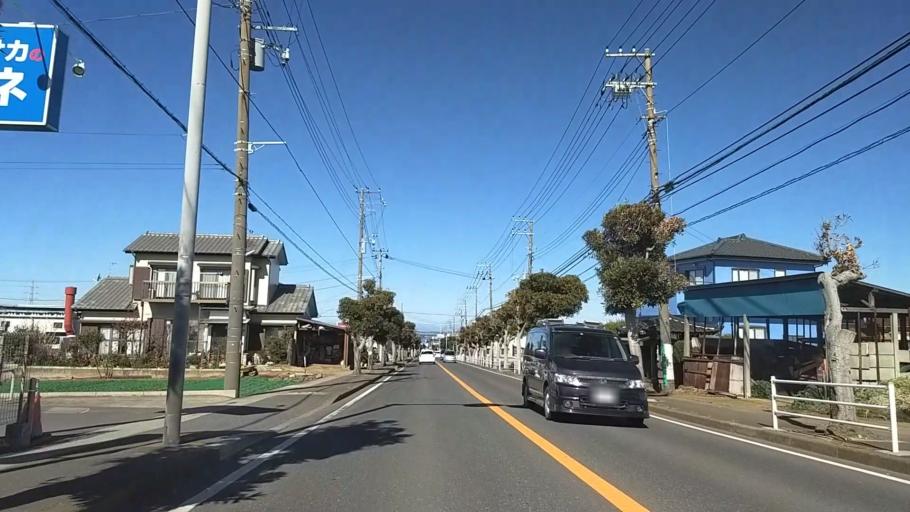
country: JP
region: Kanagawa
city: Miura
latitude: 35.1715
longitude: 139.6373
